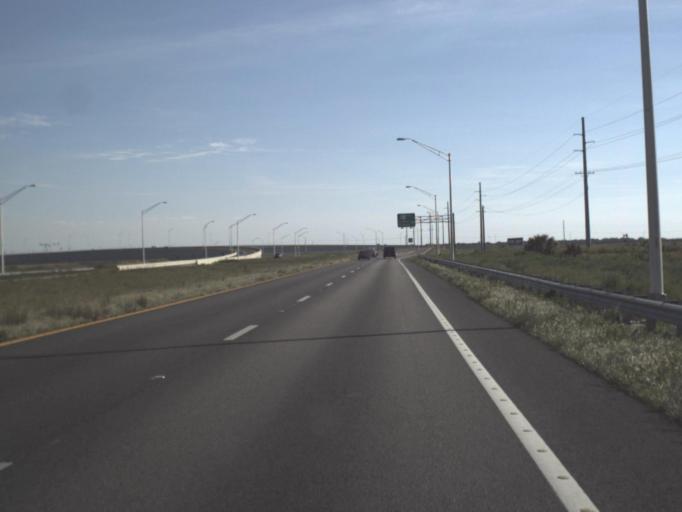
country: US
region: Florida
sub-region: Glades County
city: Moore Haven
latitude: 26.7620
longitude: -81.0832
